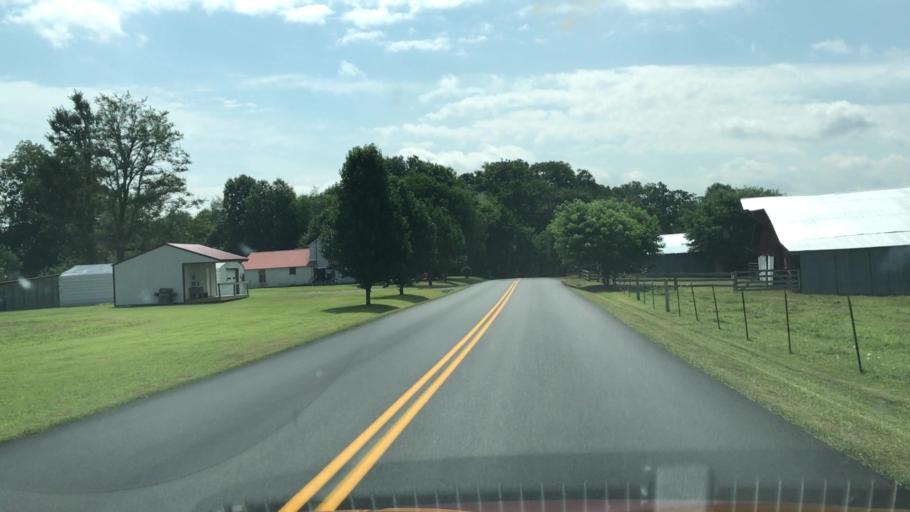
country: US
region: Kentucky
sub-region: Monroe County
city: Tompkinsville
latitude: 36.7448
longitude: -85.7620
